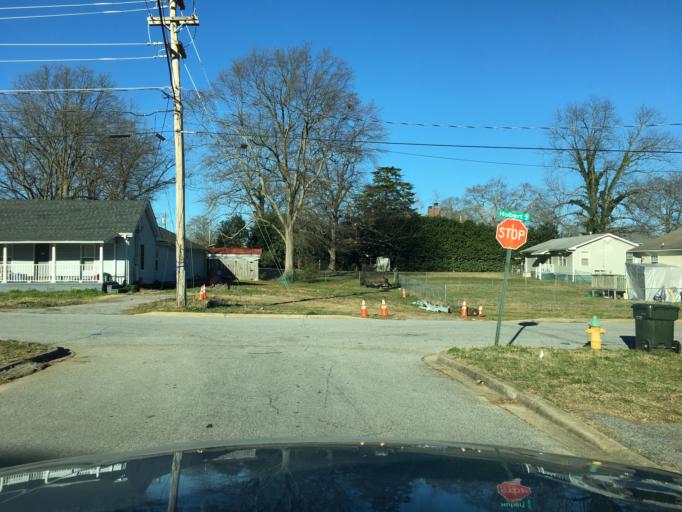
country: US
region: South Carolina
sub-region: Greenville County
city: Greer
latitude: 34.9393
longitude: -82.2347
